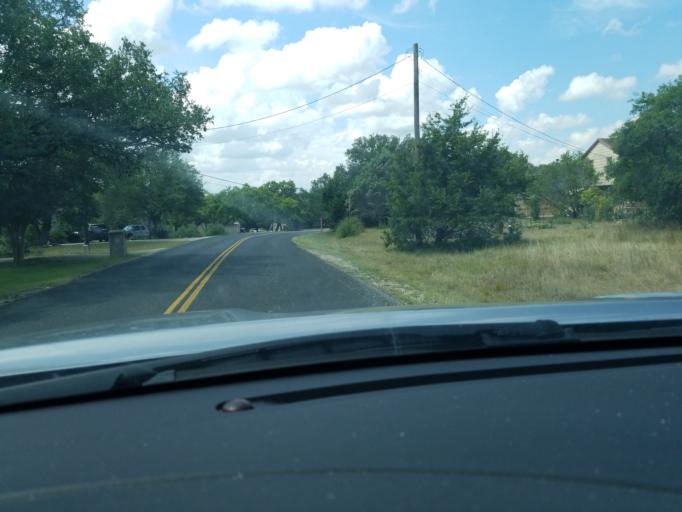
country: US
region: Texas
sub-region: Bexar County
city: Timberwood Park
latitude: 29.6866
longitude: -98.4819
